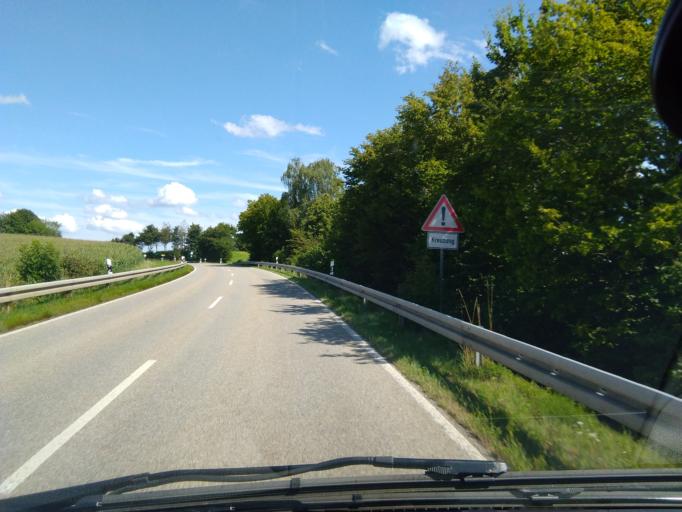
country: DE
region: Bavaria
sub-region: Upper Bavaria
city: Emmering
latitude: 47.9902
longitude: 12.0419
